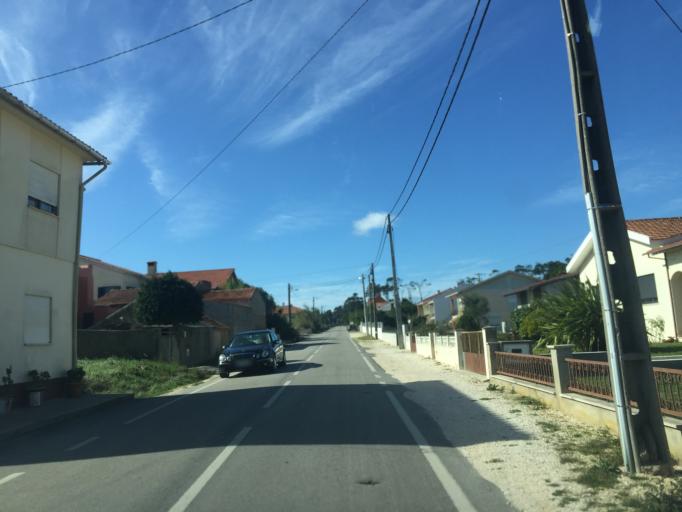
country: PT
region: Coimbra
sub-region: Figueira da Foz
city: Buarcos
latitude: 40.1914
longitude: -8.8677
